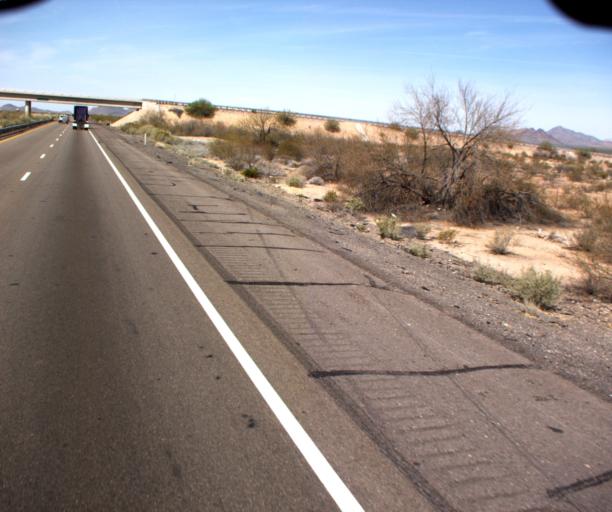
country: US
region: Arizona
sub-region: La Paz County
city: Salome
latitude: 33.5951
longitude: -113.5243
